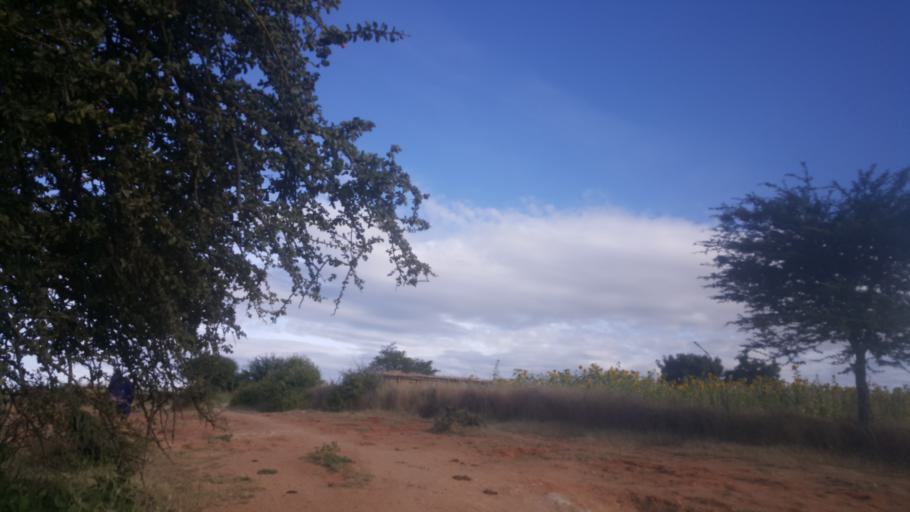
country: TZ
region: Dodoma
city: Dodoma
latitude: -6.0985
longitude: 35.5347
